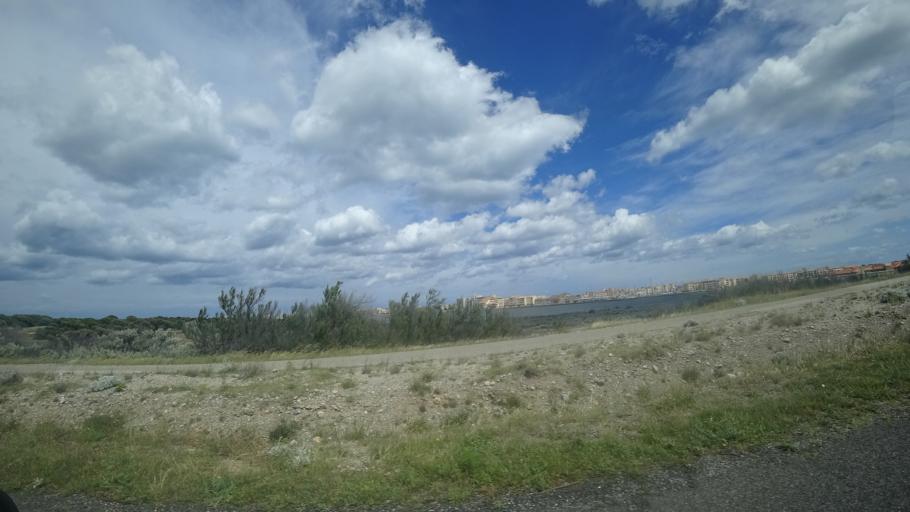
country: FR
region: Languedoc-Roussillon
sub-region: Departement de l'Aude
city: Leucate
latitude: 42.8607
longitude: 3.0296
